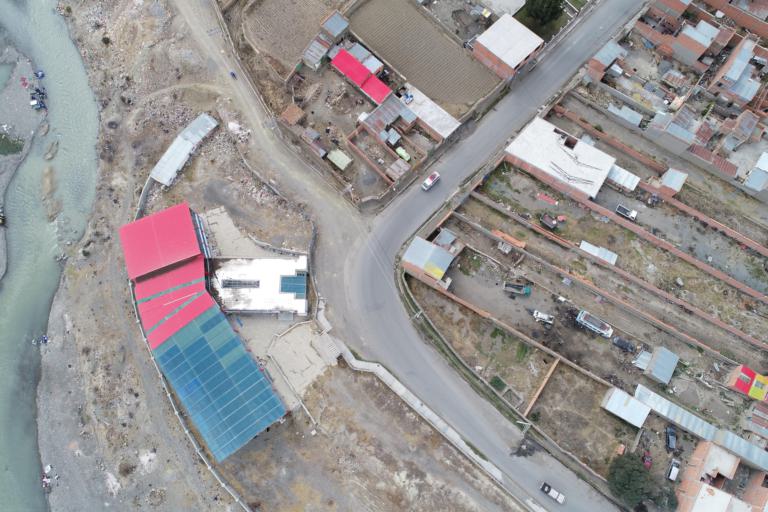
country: BO
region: La Paz
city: Achacachi
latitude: -16.0389
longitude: -68.6850
